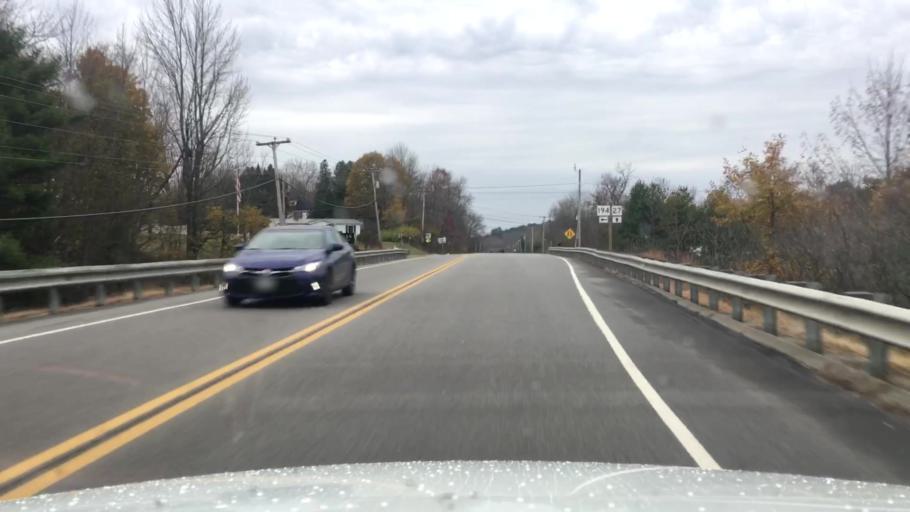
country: US
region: Maine
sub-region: Kennebec County
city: Pittston
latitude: 44.2182
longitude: -69.7560
